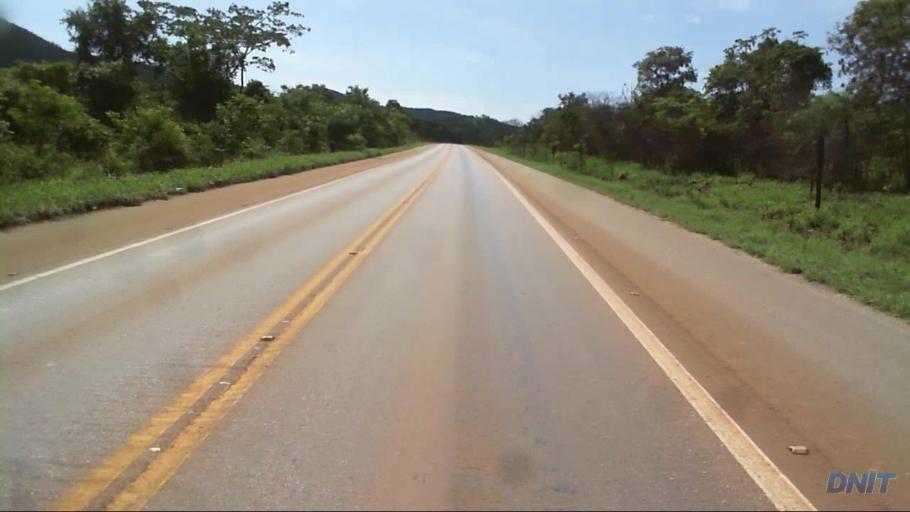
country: BR
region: Goias
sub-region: Barro Alto
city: Barro Alto
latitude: -15.1540
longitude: -48.8057
